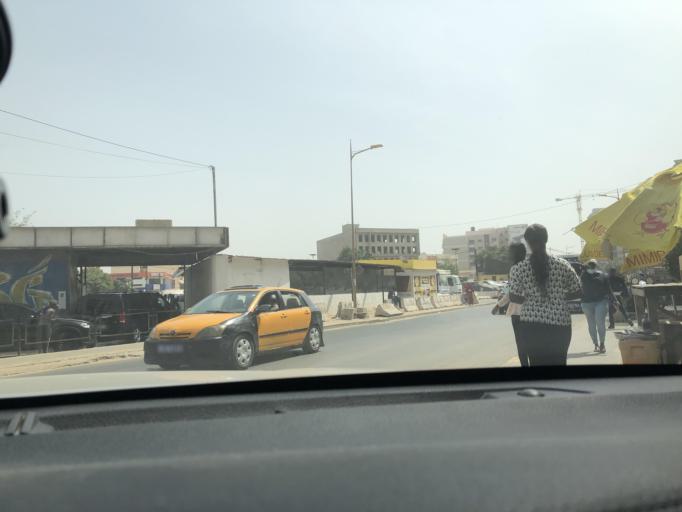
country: SN
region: Dakar
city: Mermoz Boabab
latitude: 14.7448
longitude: -17.5125
